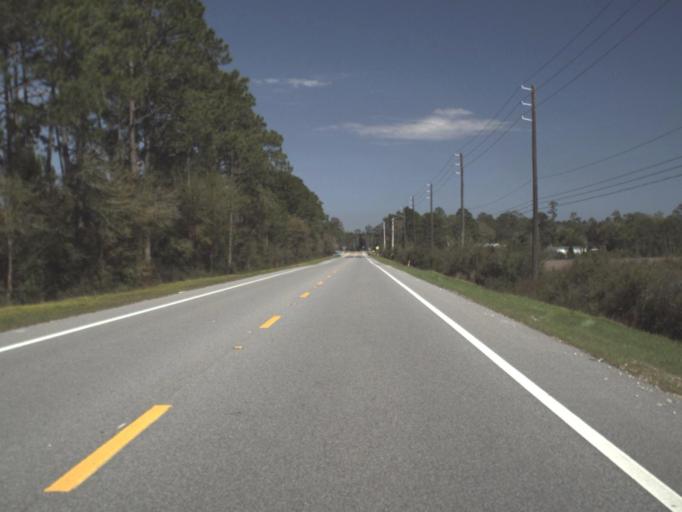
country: US
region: Florida
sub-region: Bay County
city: Lynn Haven
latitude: 30.3287
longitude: -85.7676
